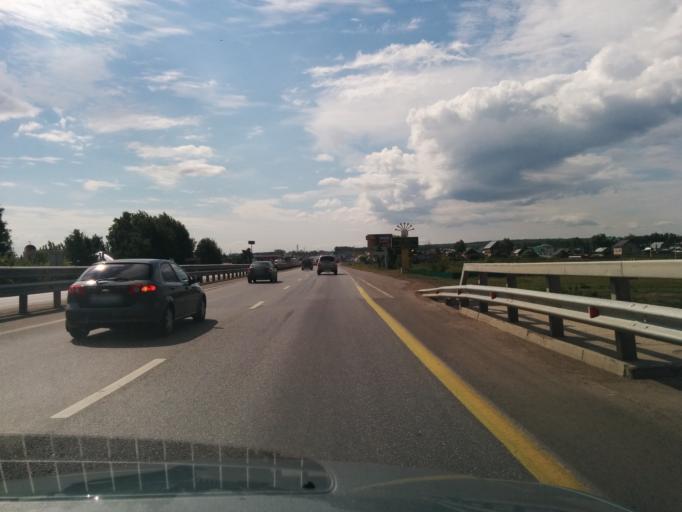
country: RU
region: Bashkortostan
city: Avdon
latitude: 54.5048
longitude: 55.9019
